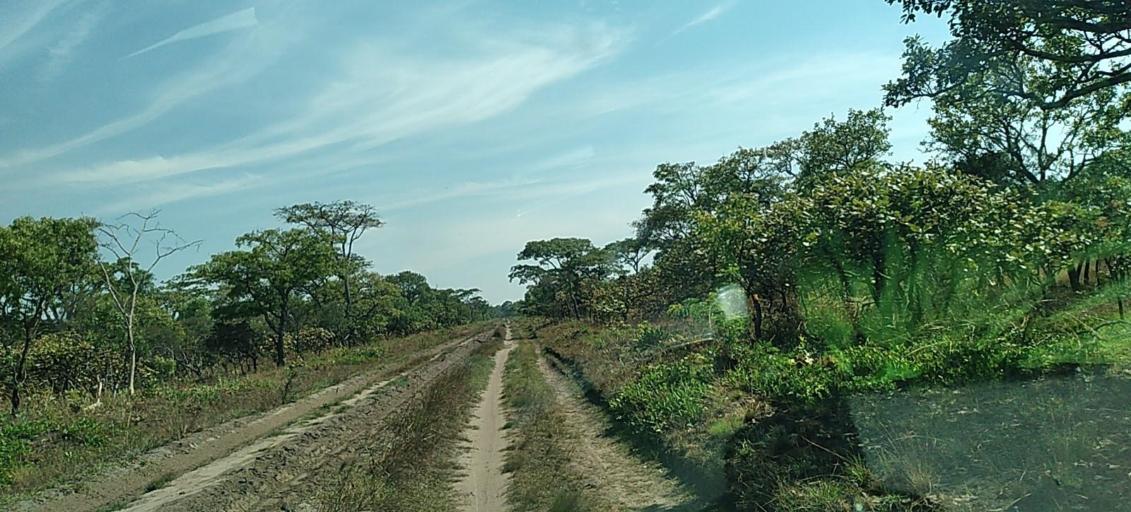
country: ZM
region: North-Western
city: Mwinilunga
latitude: -11.8031
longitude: 25.1656
